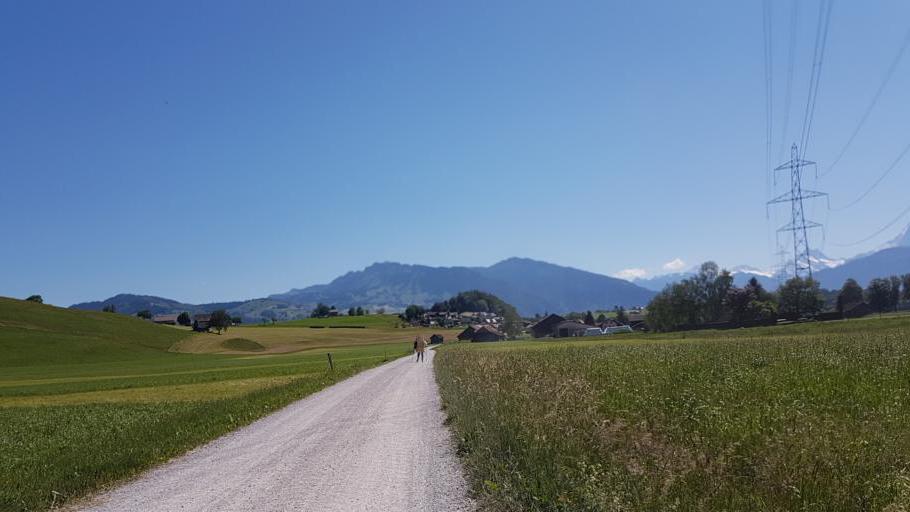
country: CH
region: Bern
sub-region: Frutigen-Niedersimmental District
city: Wimmis
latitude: 46.7047
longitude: 7.6144
